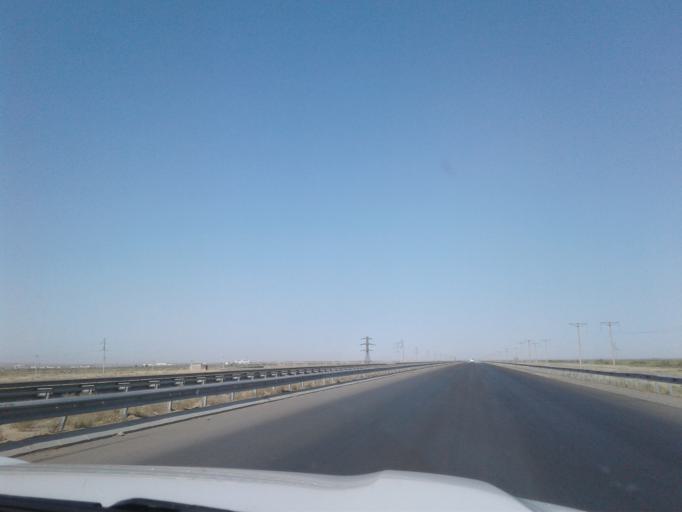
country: TM
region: Balkan
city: Gazanjyk
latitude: 39.2682
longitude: 55.5293
